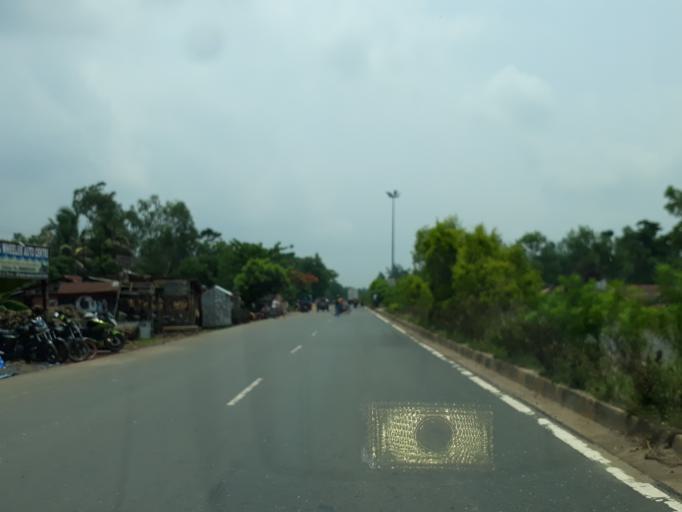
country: IN
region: West Bengal
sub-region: Purba Medinipur
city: Monoharpur
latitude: 22.1024
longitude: 88.0261
